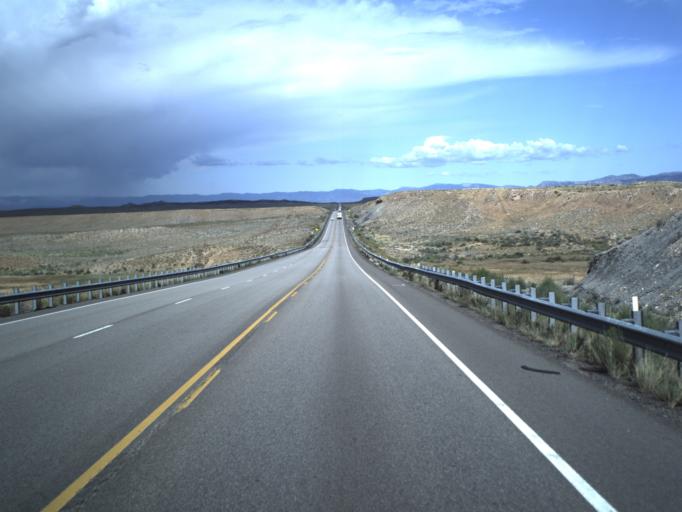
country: US
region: Utah
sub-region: Carbon County
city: East Carbon City
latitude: 39.5131
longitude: -110.5439
